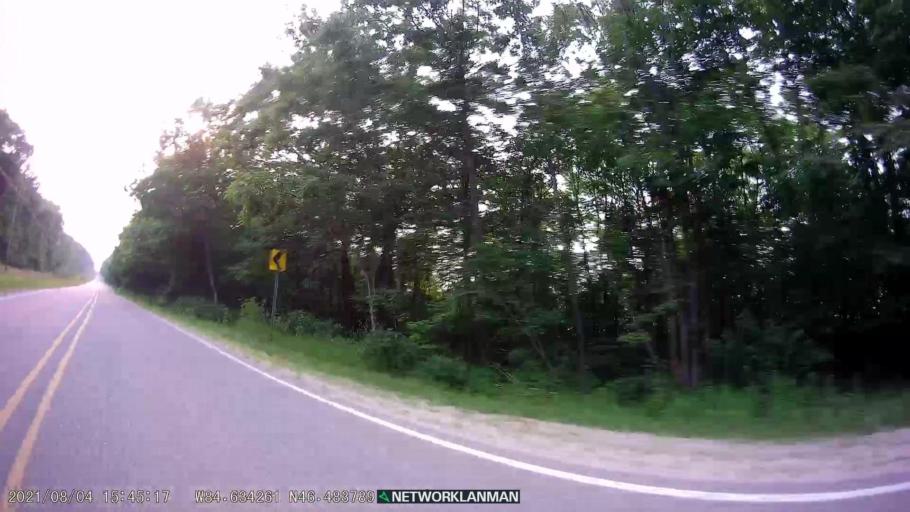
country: US
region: Michigan
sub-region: Chippewa County
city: Sault Ste. Marie
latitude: 46.4838
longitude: -84.6346
